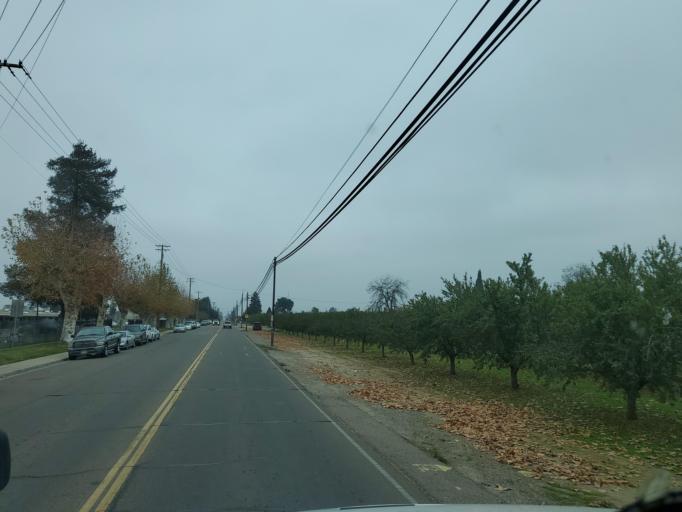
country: US
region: California
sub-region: Stanislaus County
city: Hughson
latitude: 37.5948
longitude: -120.8607
